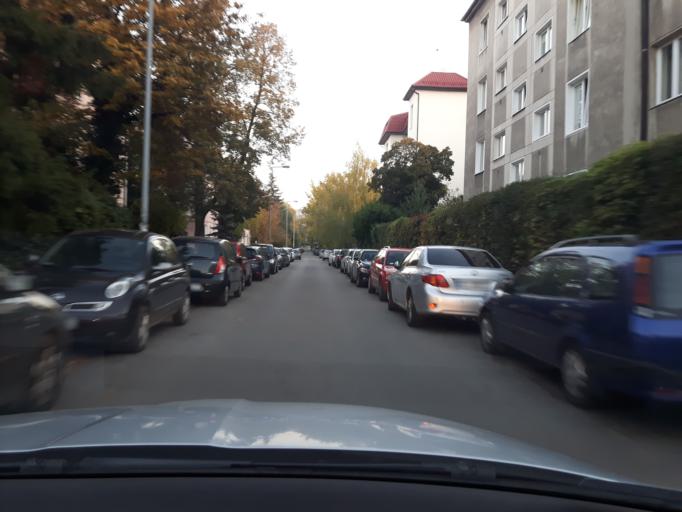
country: PL
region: Masovian Voivodeship
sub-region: Warszawa
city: Mokotow
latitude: 52.1931
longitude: 21.0172
